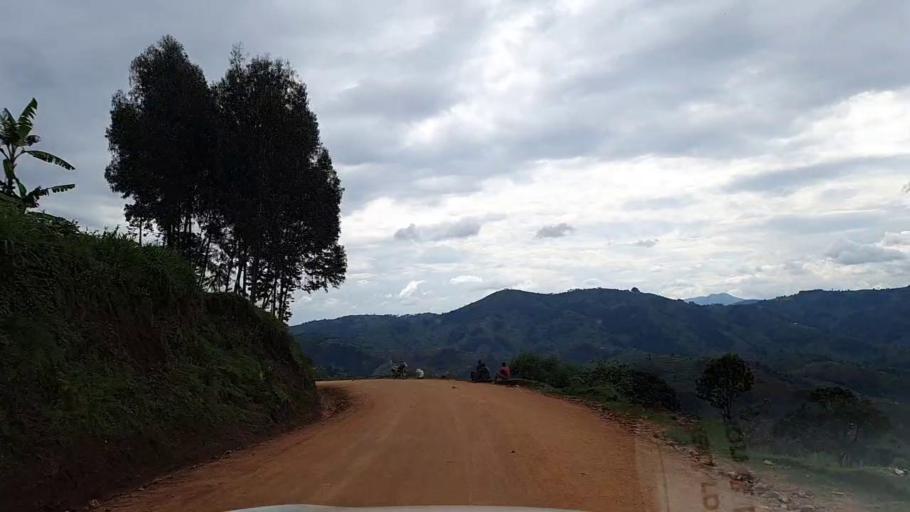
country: RW
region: Southern Province
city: Nzega
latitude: -2.4012
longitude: 29.4538
